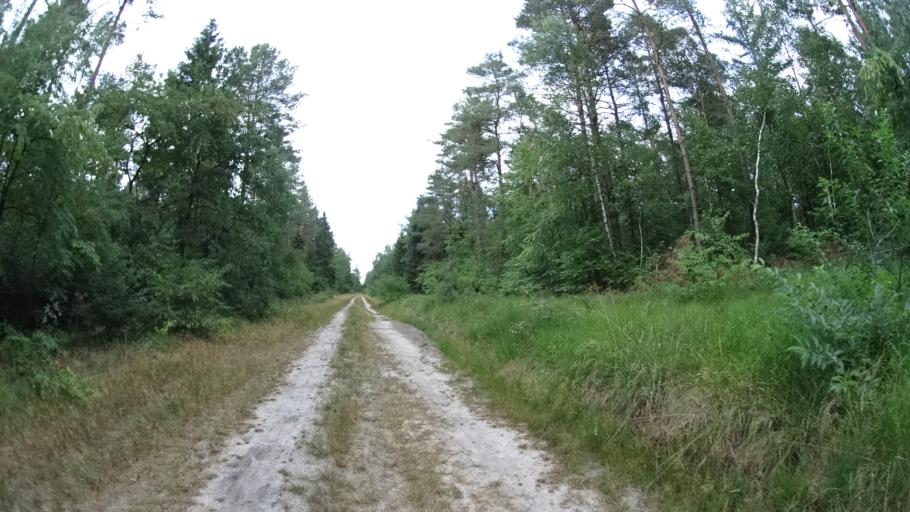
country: DE
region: Lower Saxony
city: Handeloh
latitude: 53.2005
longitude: 9.8786
